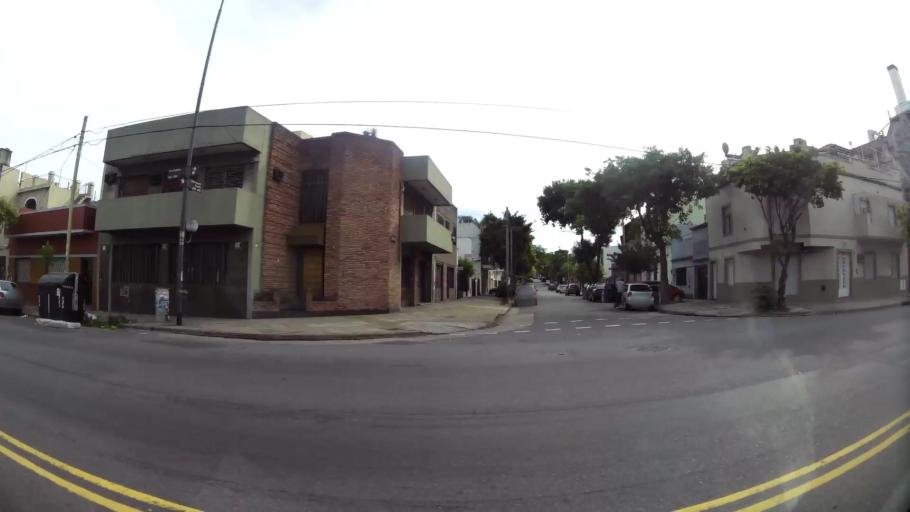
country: AR
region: Buenos Aires F.D.
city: Villa Santa Rita
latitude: -34.6406
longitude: -58.4638
